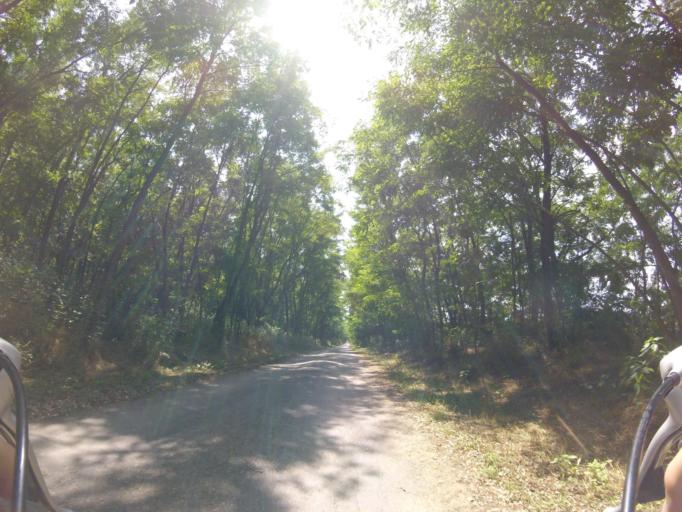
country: SK
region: Nitriansky
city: Sahy
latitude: 48.0424
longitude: 18.8459
